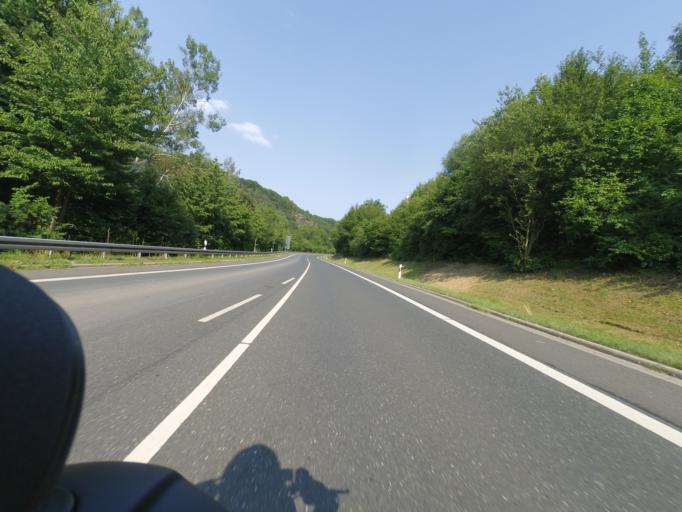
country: DE
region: Saxony
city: Waldheim
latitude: 51.0785
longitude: 13.0204
